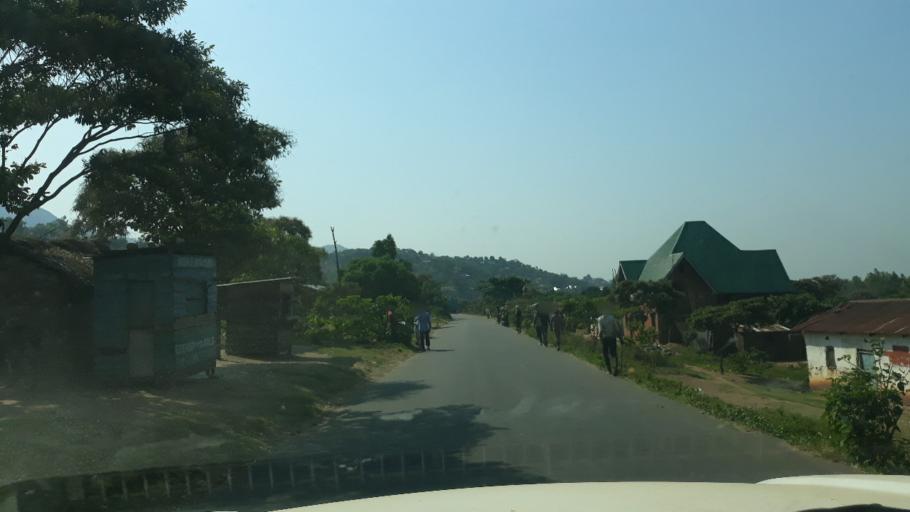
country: CD
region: South Kivu
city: Uvira
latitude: -3.2459
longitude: 29.1611
